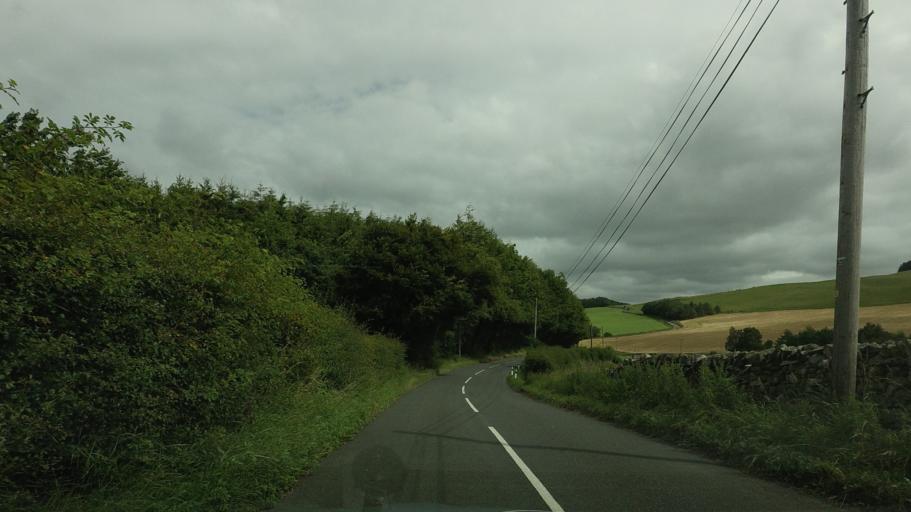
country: GB
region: Scotland
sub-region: The Scottish Borders
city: Selkirk
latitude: 55.5129
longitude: -2.9342
